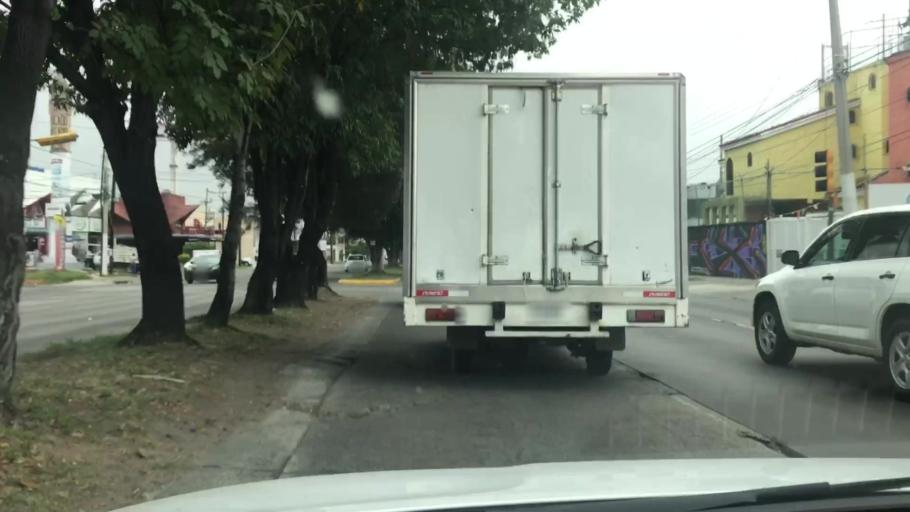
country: MX
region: Jalisco
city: Guadalajara
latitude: 20.6366
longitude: -103.4219
